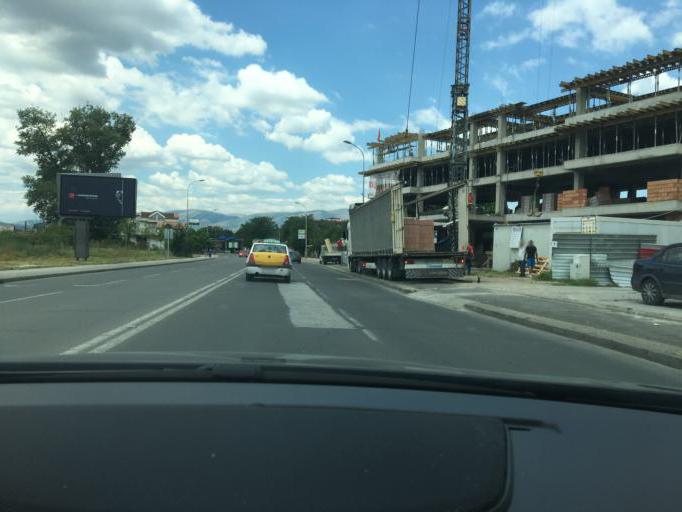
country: MK
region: Saraj
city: Saraj
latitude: 42.0065
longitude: 21.3430
